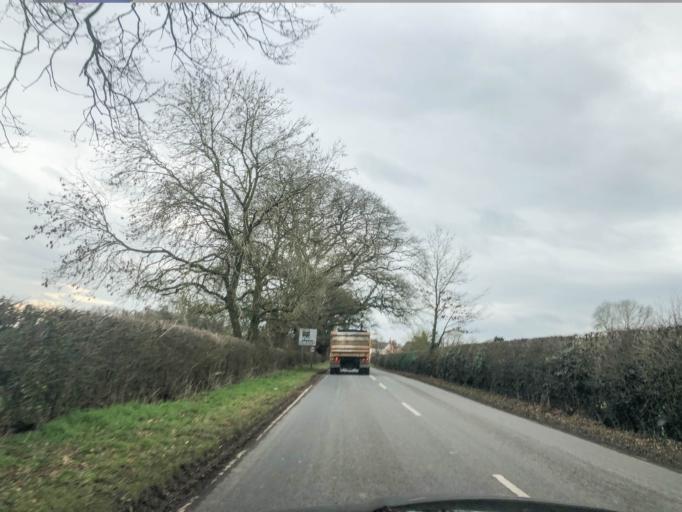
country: GB
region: England
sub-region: Warwickshire
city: Wroxall
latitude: 52.3080
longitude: -1.6819
